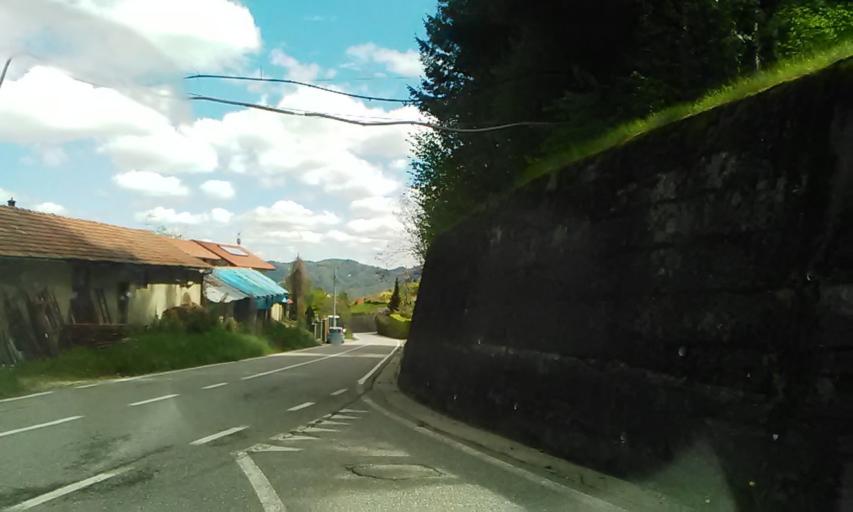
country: IT
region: Piedmont
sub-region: Provincia di Vercelli
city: Cellio
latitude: 45.7586
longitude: 8.3097
